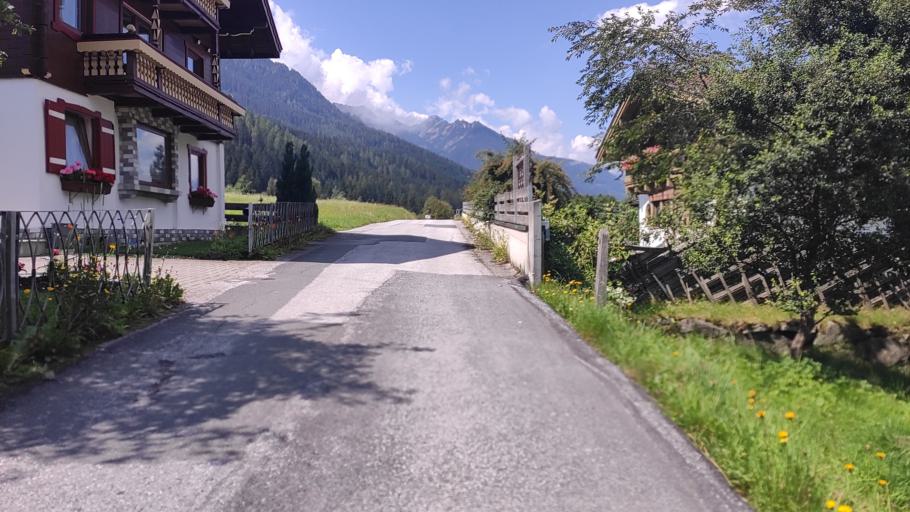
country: AT
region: Salzburg
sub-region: Politischer Bezirk Zell am See
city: Neukirchen am Grossvenediger
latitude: 47.2517
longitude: 12.3072
